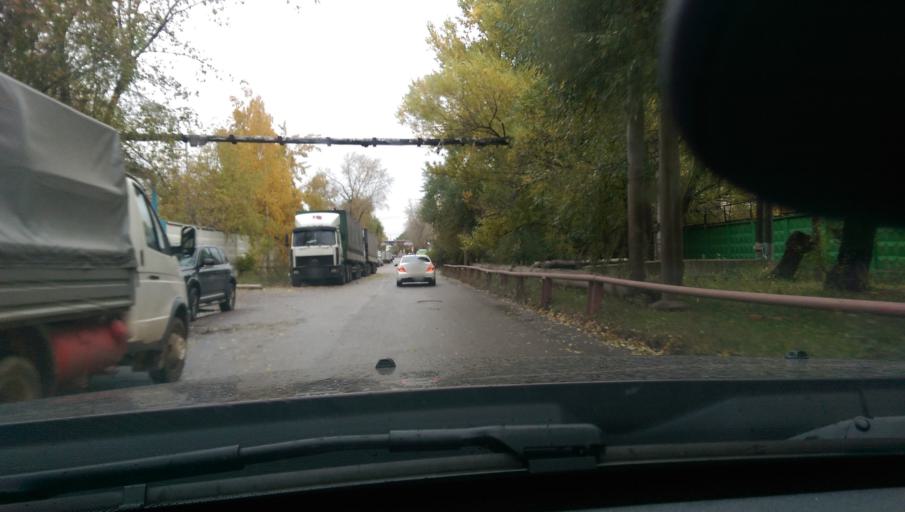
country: RU
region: Moscow
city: Altuf'yevskiy
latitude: 55.8882
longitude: 37.5735
